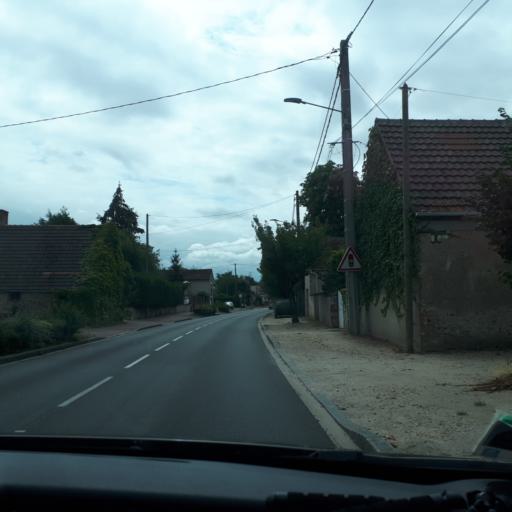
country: FR
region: Centre
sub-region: Departement du Loiret
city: Saint-Pere-sur-Loire
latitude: 47.7761
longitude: 2.3732
